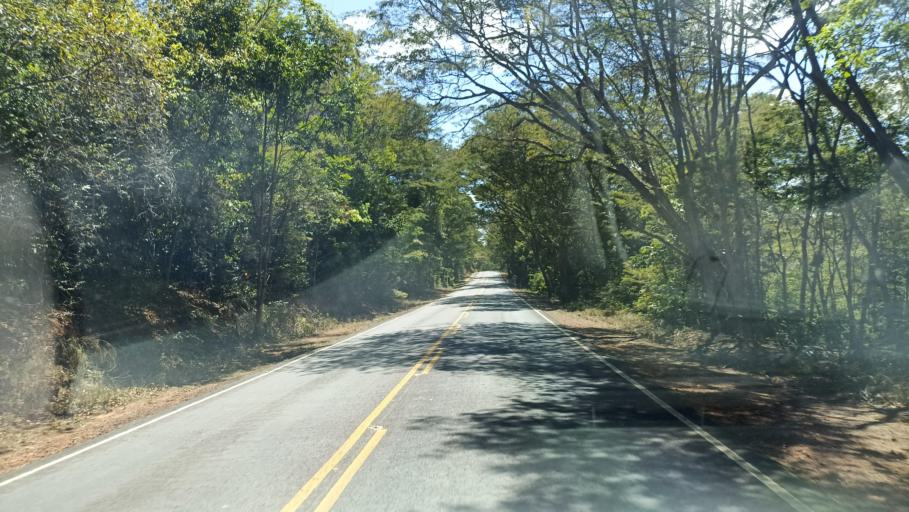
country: BR
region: Bahia
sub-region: Andarai
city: Vera Cruz
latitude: -12.7745
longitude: -41.3302
